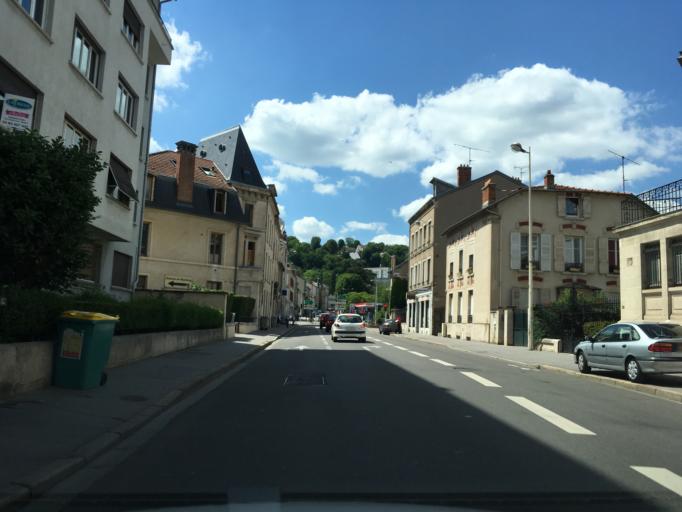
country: FR
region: Lorraine
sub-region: Departement de Meurthe-et-Moselle
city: Maxeville
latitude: 48.6919
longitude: 6.1696
